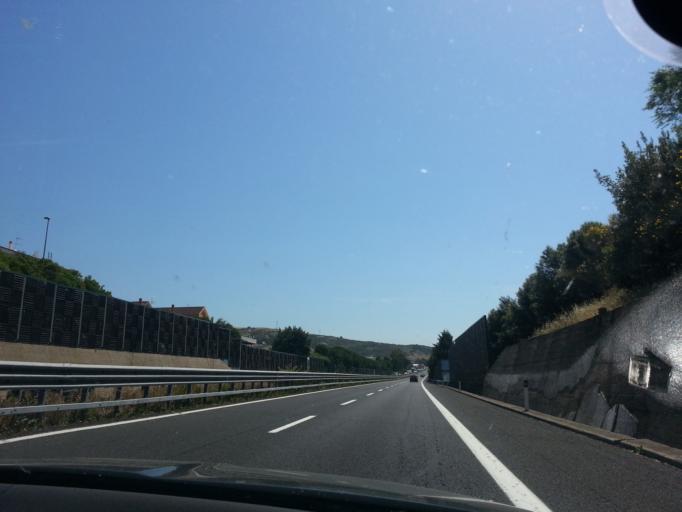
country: IT
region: Latium
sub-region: Citta metropolitana di Roma Capitale
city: Santa Marinella
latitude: 42.0445
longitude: 11.8795
